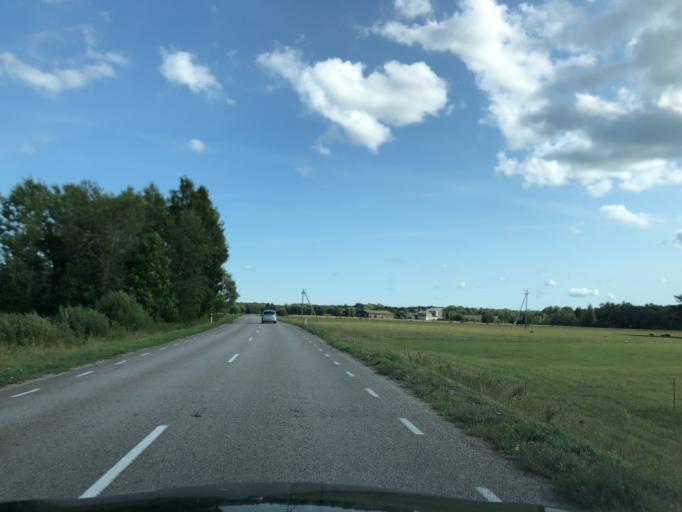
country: EE
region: Hiiumaa
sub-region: Kaerdla linn
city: Kardla
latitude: 58.7140
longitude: 22.5770
